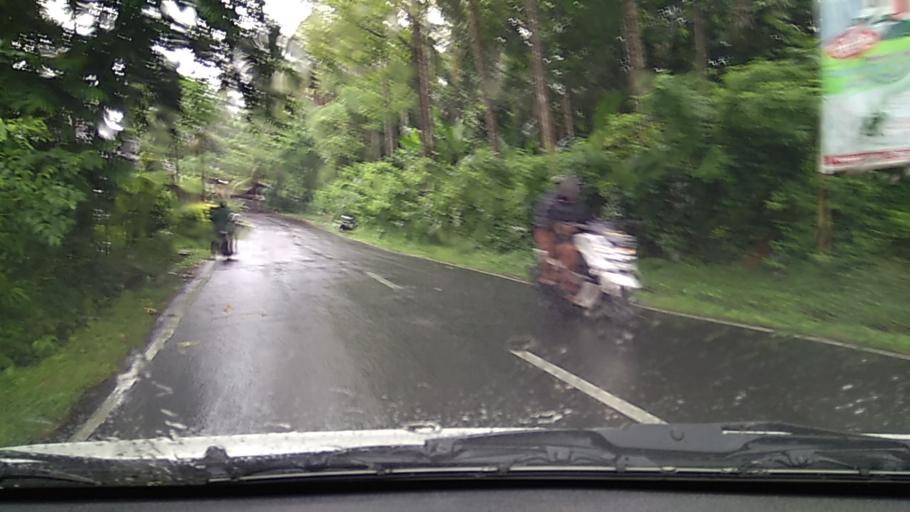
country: ID
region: Bali
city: Banjar Timbrah
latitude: -8.4745
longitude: 115.6187
